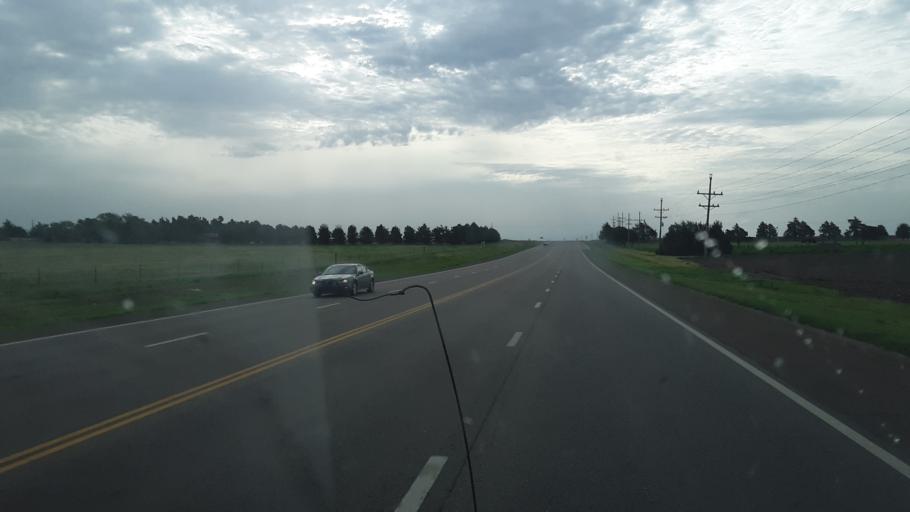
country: US
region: Kansas
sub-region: Finney County
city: Garden City
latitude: 37.9600
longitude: -100.7975
